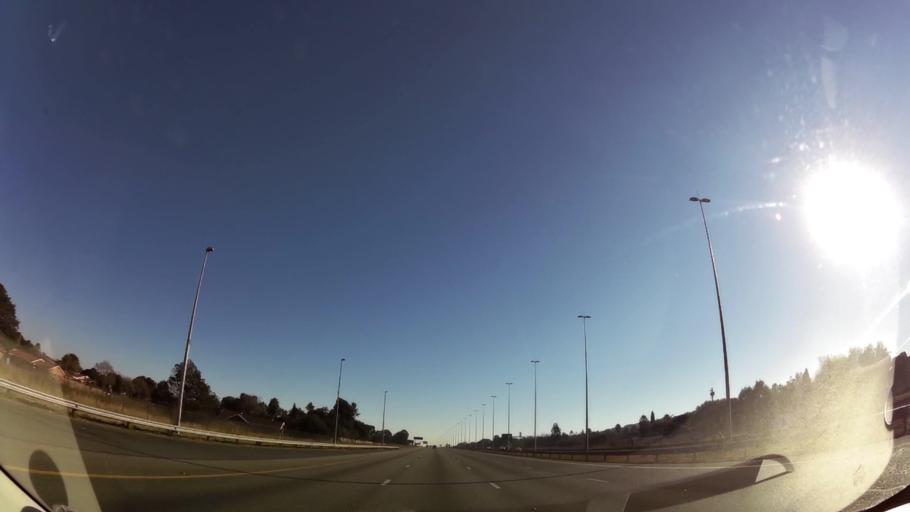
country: ZA
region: Gauteng
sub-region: City of Tshwane Metropolitan Municipality
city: Centurion
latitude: -25.8498
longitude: 28.2511
